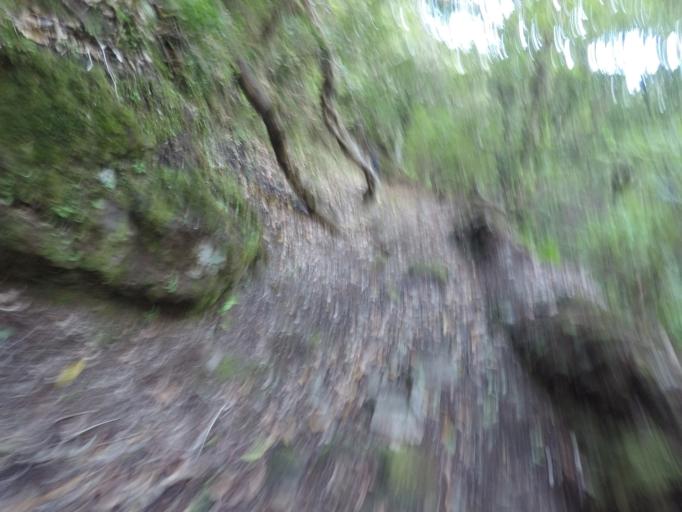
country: PT
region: Madeira
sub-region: Camara de Lobos
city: Curral das Freiras
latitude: 32.7733
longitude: -16.9794
